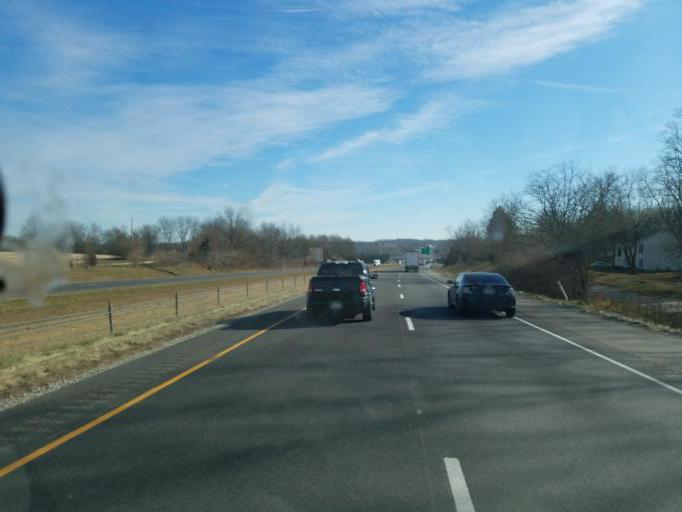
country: US
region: Indiana
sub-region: Wayne County
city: Richmond
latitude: 39.8705
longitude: -84.8678
